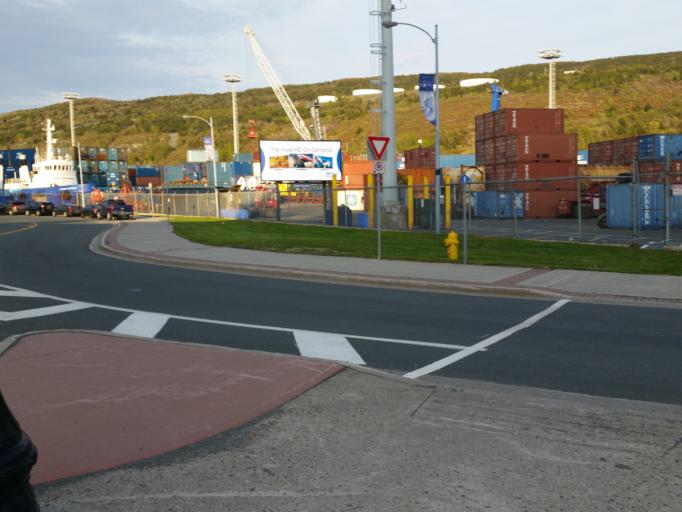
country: CA
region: Newfoundland and Labrador
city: St. John's
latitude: 47.5590
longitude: -52.7117
